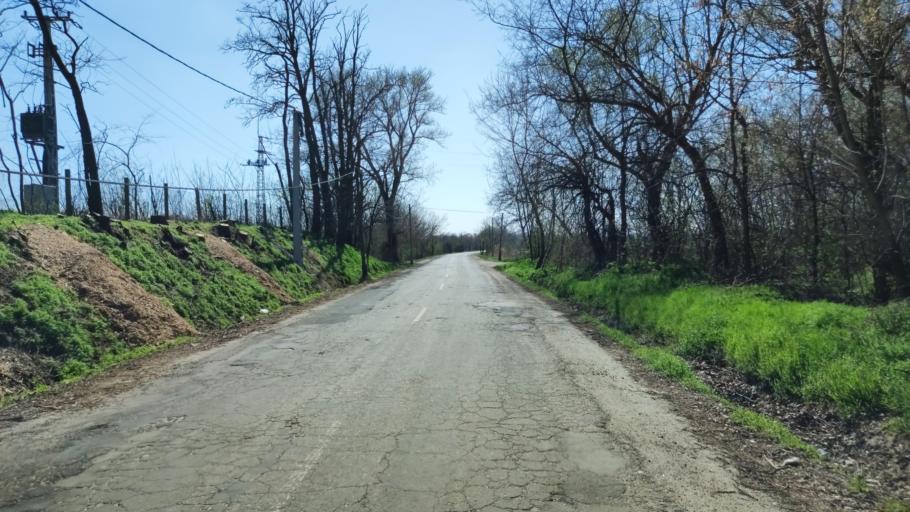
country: HU
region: Pest
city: Szod
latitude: 47.7233
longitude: 19.1955
